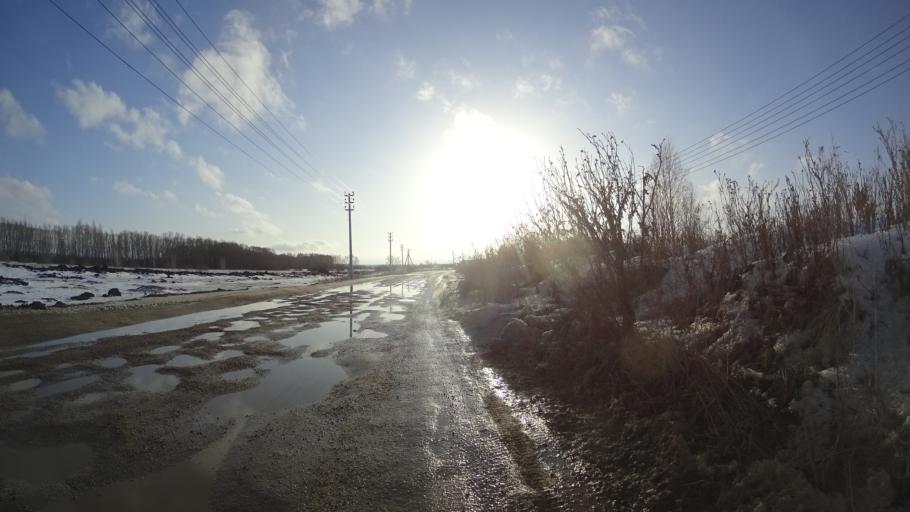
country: RU
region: Chelyabinsk
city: Sargazy
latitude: 55.1066
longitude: 61.2682
